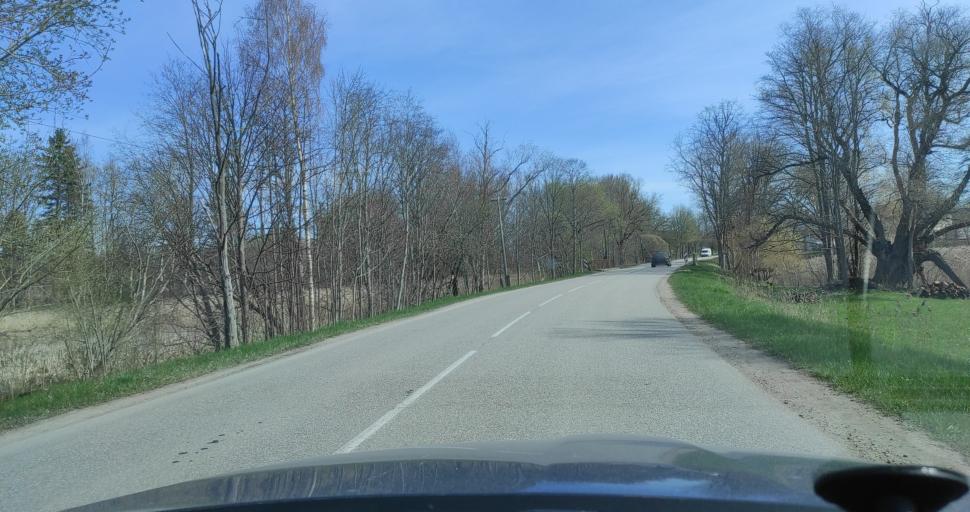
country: LV
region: Talsu Rajons
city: Talsi
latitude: 57.2248
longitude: 22.5154
